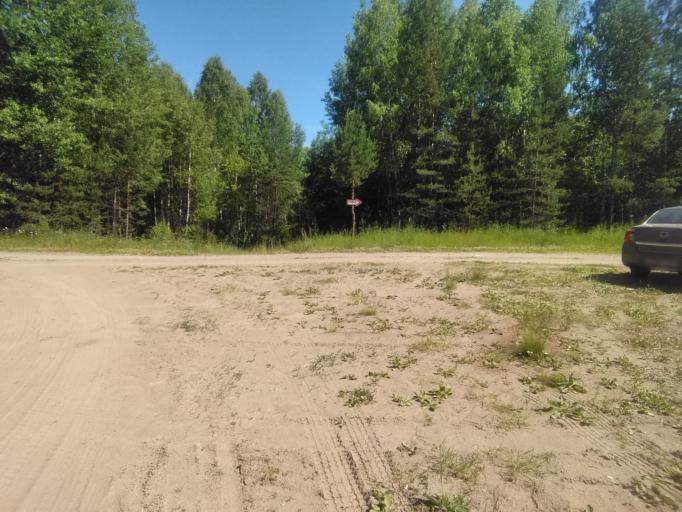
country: RU
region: Perm
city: Foki
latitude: 56.5118
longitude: 54.5775
